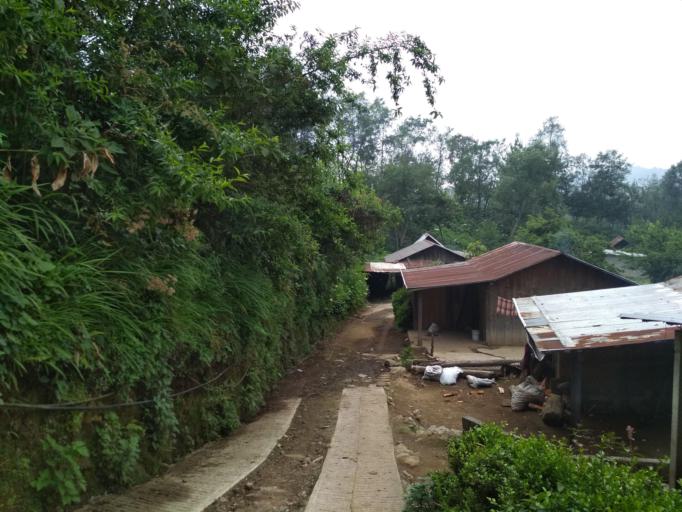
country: MX
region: Veracruz
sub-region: La Perla
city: Chilapa
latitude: 18.9876
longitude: -97.1498
